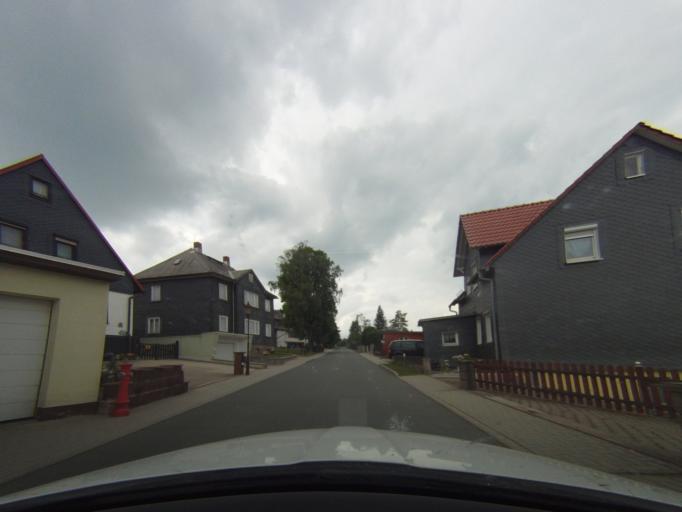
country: DE
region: Thuringia
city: Drobischau
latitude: 50.6303
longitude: 11.0723
